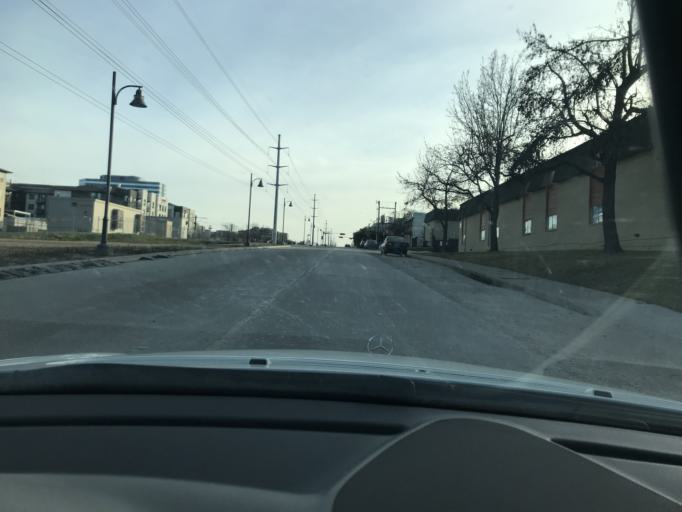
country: US
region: Texas
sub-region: Dallas County
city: University Park
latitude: 32.8897
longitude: -96.7653
